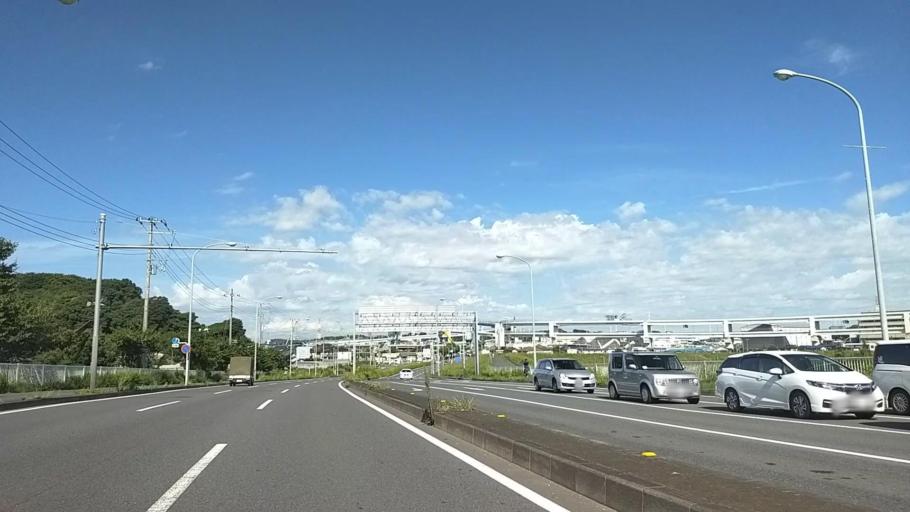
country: JP
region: Kanagawa
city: Yokohama
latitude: 35.5126
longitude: 139.6000
